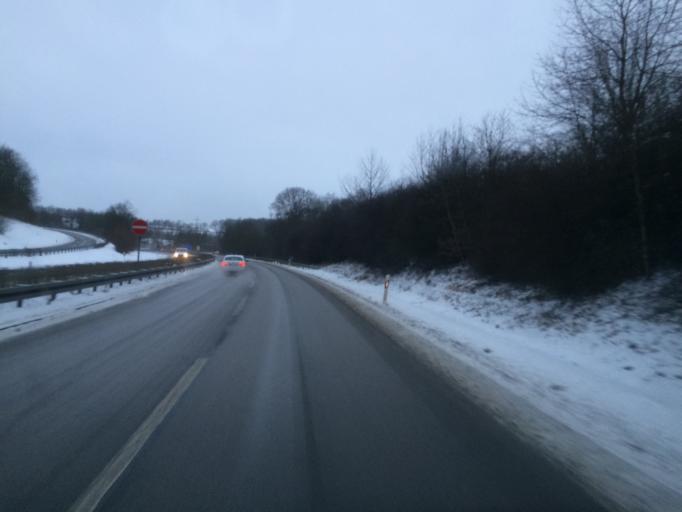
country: DE
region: Bavaria
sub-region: Upper Palatinate
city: Pentling
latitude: 49.0023
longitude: 12.0692
